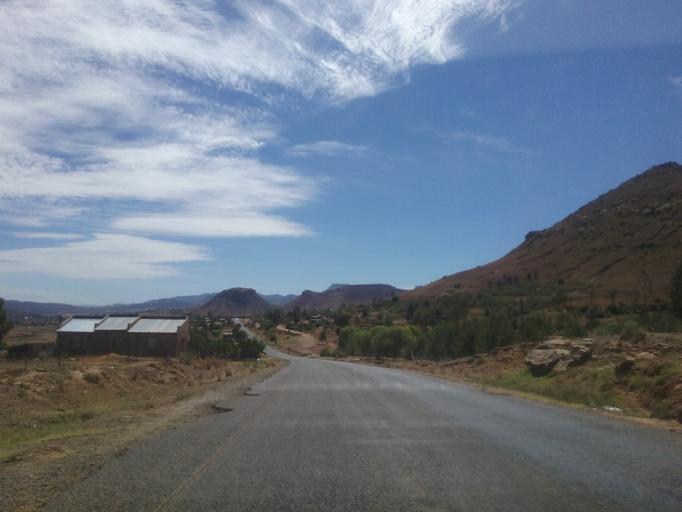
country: LS
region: Mohale's Hoek District
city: Mohale's Hoek
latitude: -30.1864
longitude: 27.4210
